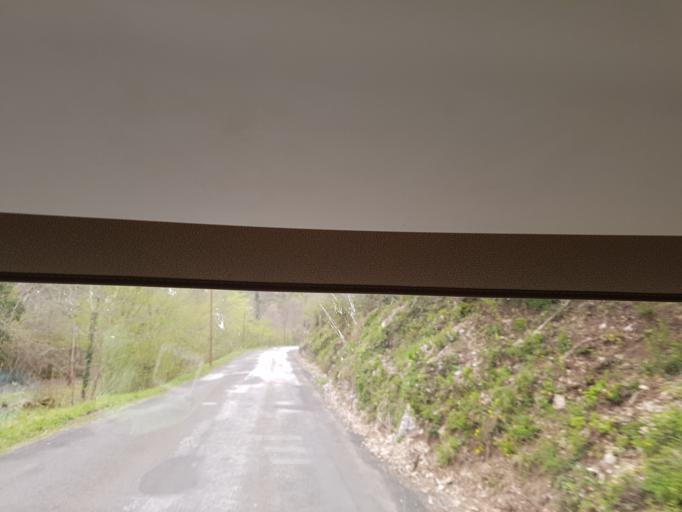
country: FR
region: Languedoc-Roussillon
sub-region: Departement de l'Aude
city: Quillan
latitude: 42.7745
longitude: 2.1791
